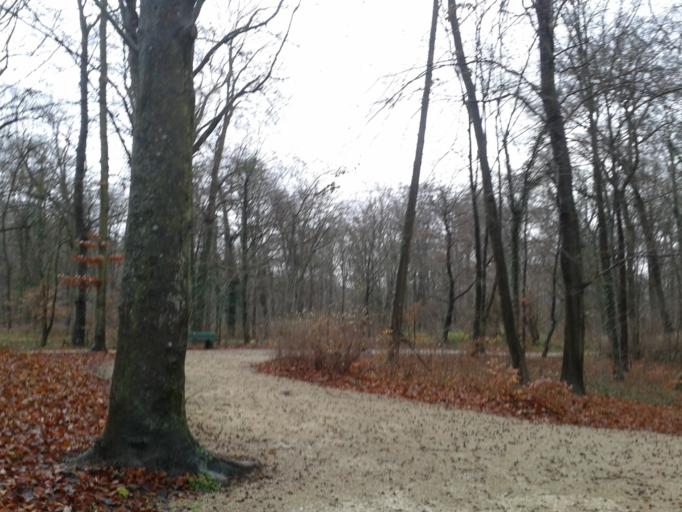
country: DE
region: Bavaria
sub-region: Upper Franconia
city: Bamberg
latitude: 49.8807
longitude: 10.8989
